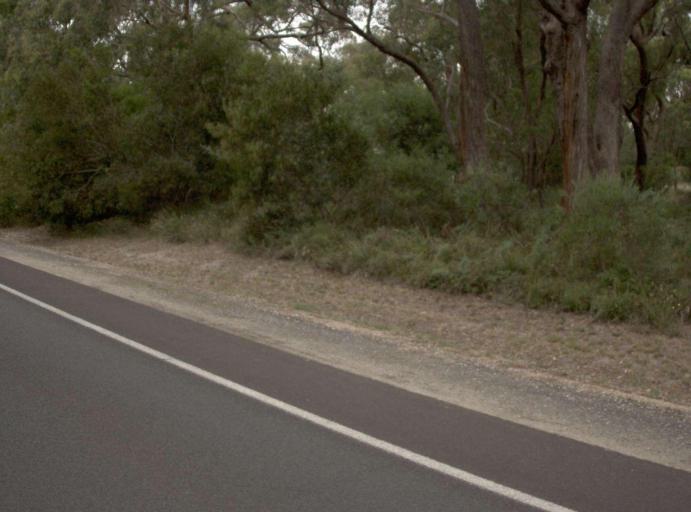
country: AU
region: Victoria
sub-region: Wellington
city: Sale
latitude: -38.1892
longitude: 147.0800
